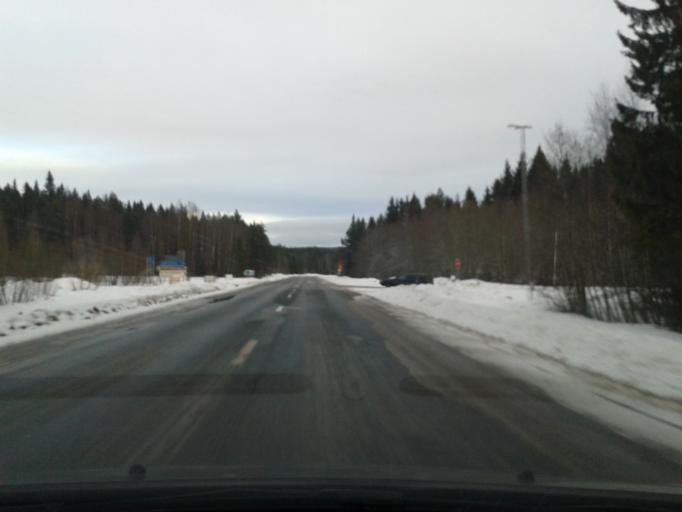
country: SE
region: Vaesternorrland
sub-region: Solleftea Kommun
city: As
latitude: 63.4365
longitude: 16.9347
